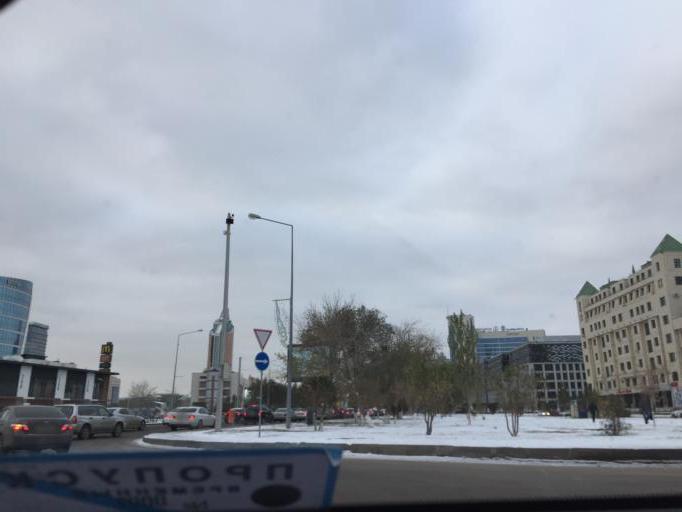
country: KZ
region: Astana Qalasy
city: Astana
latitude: 51.1382
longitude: 71.4165
